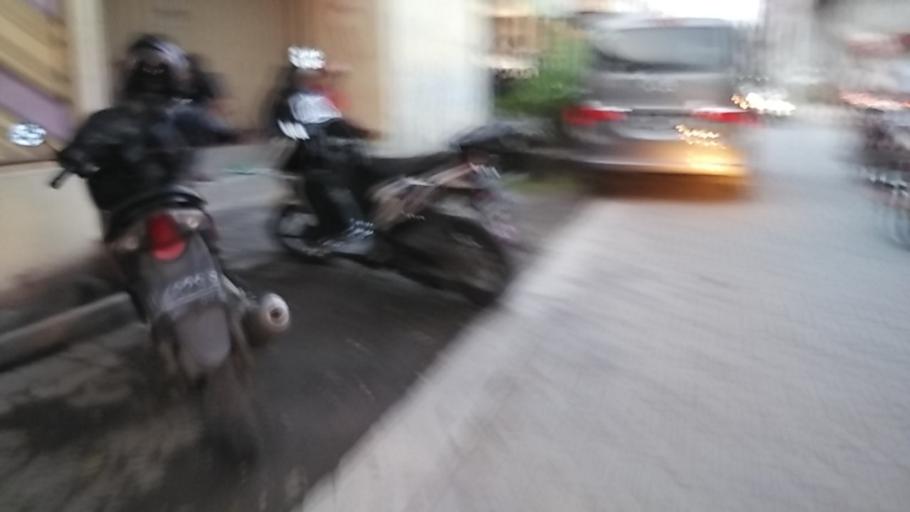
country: ID
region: Central Java
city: Semarang
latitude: -6.9822
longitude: 110.4554
